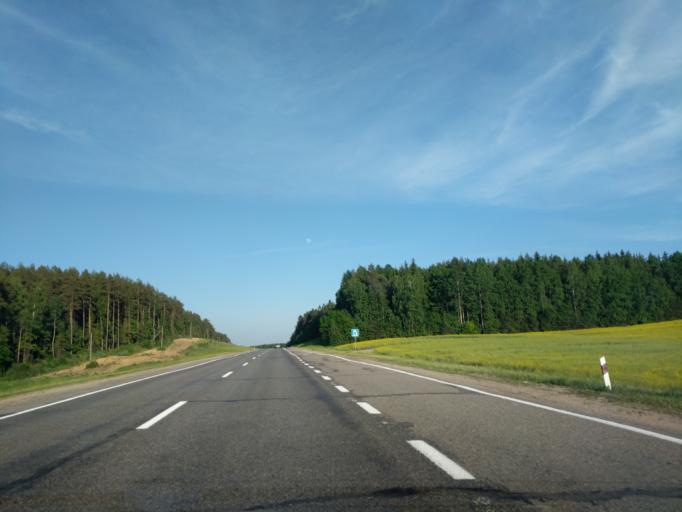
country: BY
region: Grodnenskaya
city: Ashmyany
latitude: 54.4193
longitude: 26.0189
